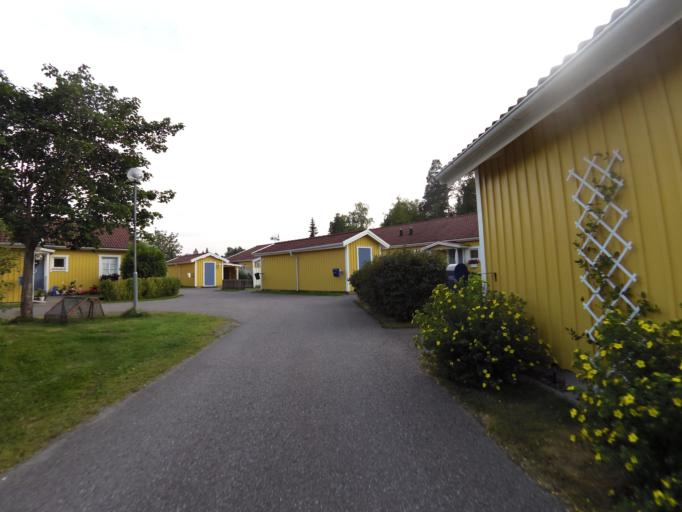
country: SE
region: Gaevleborg
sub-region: Gavle Kommun
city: Gavle
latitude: 60.6994
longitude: 17.0959
